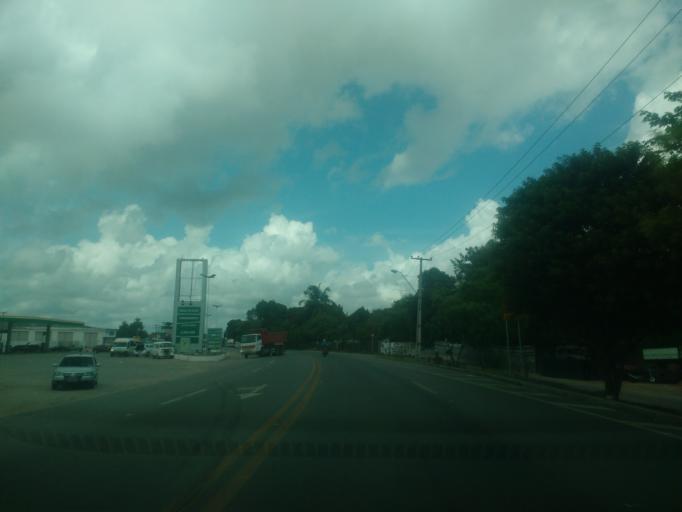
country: BR
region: Alagoas
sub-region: Satuba
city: Satuba
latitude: -9.5647
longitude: -35.7888
